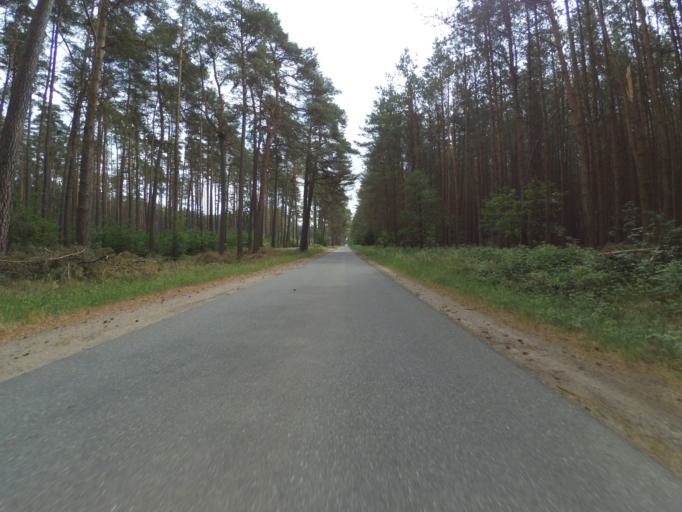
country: DE
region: Mecklenburg-Vorpommern
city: Malchow
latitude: 53.5600
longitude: 12.3987
